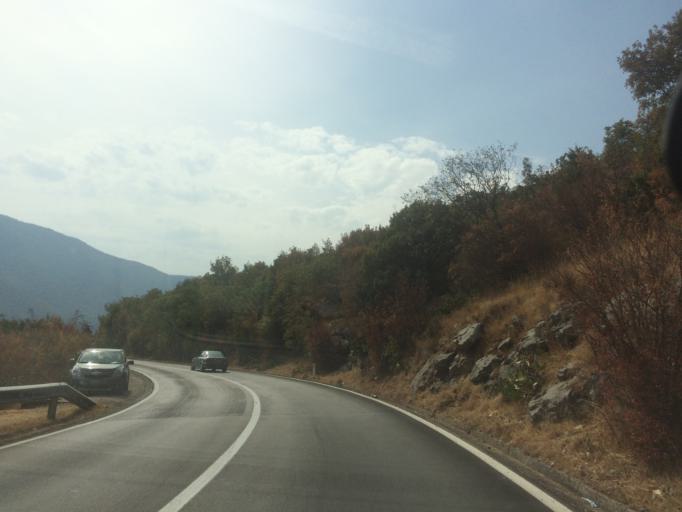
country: ME
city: Dobrota
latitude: 42.4854
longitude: 18.7405
